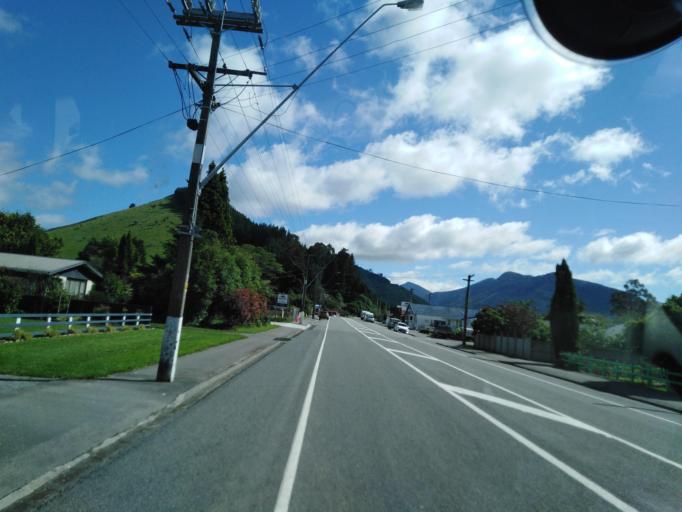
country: NZ
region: Nelson
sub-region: Nelson City
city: Nelson
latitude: -41.2291
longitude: 173.5826
